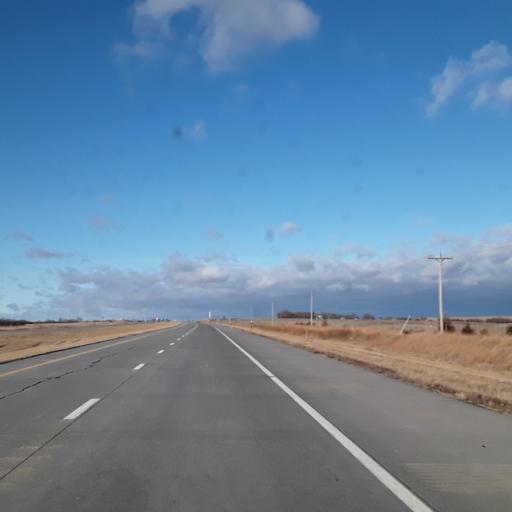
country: US
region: Kansas
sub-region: Republic County
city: Belleville
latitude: 39.8890
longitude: -97.6142
